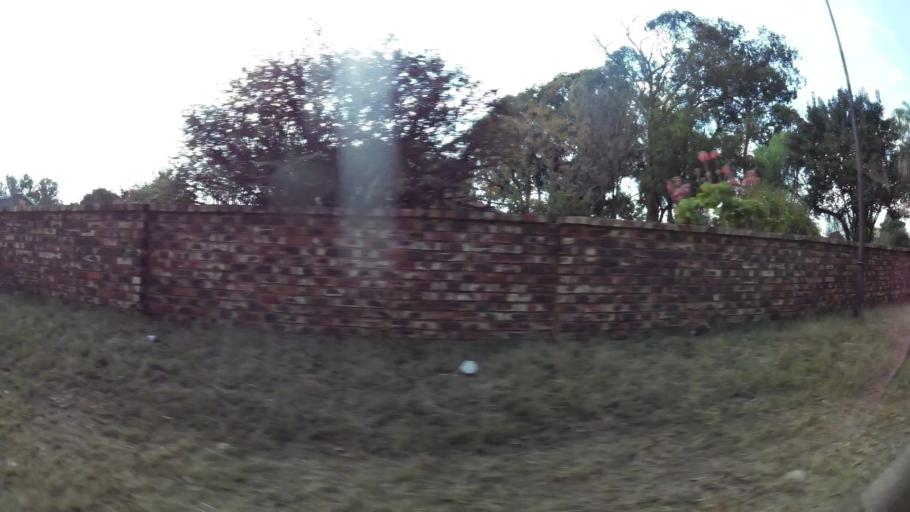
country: ZA
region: Gauteng
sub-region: Ekurhuleni Metropolitan Municipality
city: Benoni
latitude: -26.1054
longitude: 28.3665
